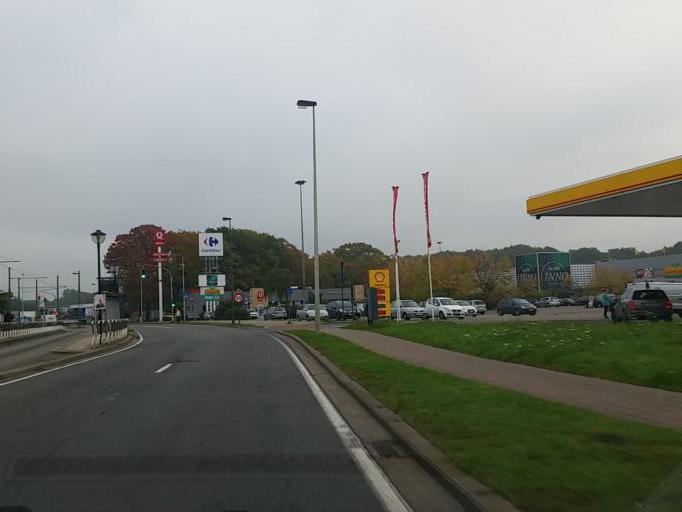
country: BE
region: Flanders
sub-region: Provincie Antwerpen
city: Schoten
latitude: 51.2583
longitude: 4.4629
